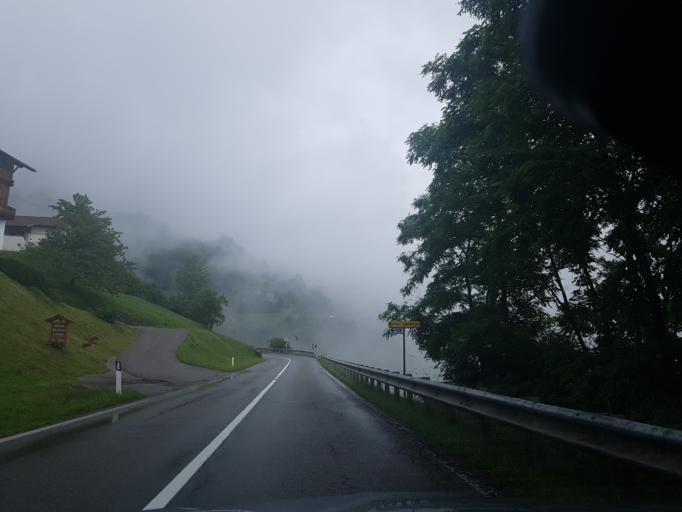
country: IT
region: Trentino-Alto Adige
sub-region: Bolzano
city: Laion
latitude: 46.5976
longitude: 11.6165
